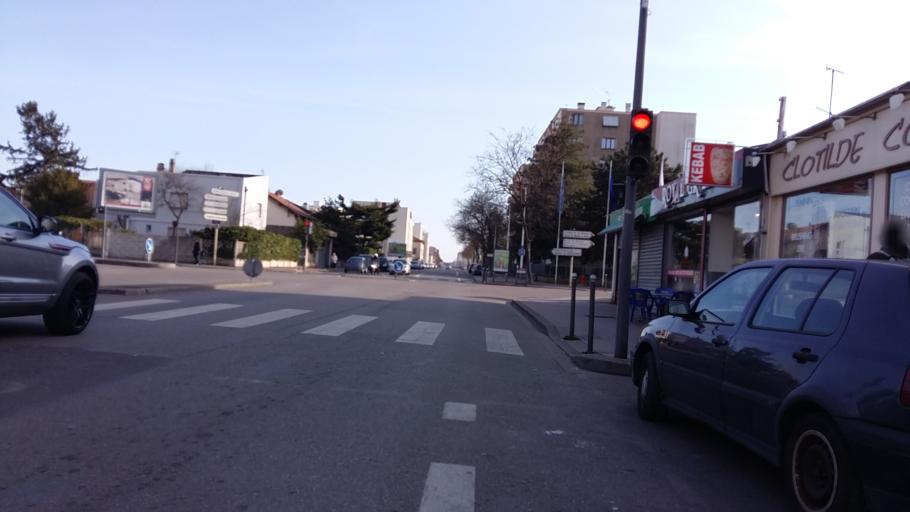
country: FR
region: Rhone-Alpes
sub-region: Departement du Rhone
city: Saint-Fons
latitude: 45.7270
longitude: 4.8622
